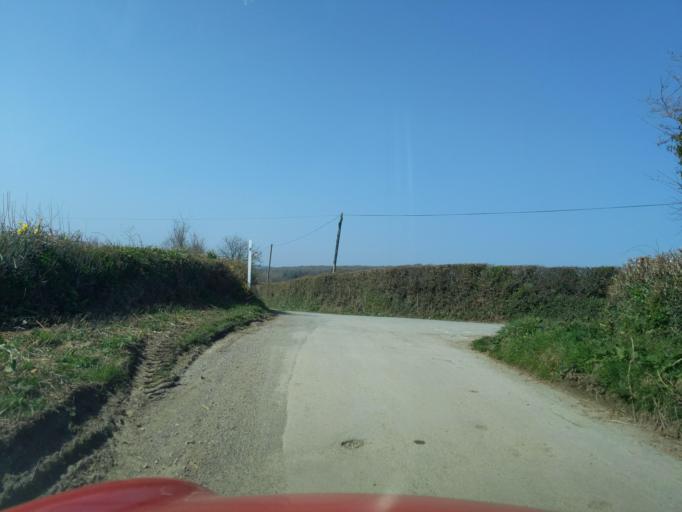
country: GB
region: England
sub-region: Devon
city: Bere Alston
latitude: 50.4426
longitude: -4.1469
